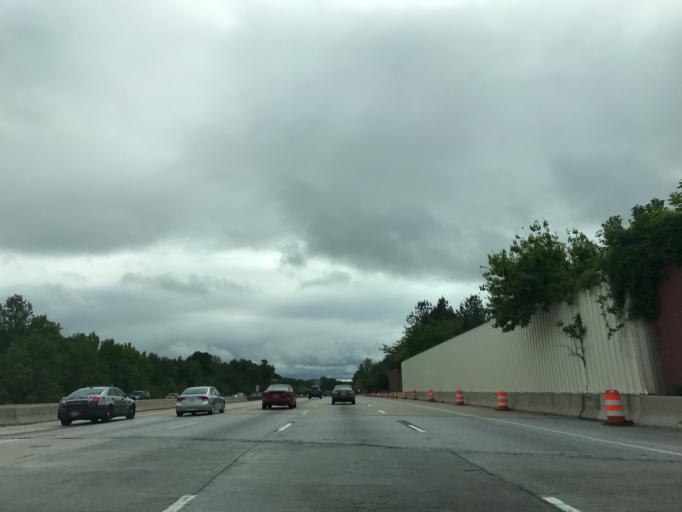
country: US
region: Maryland
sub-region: Prince George's County
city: Bowie
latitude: 38.9511
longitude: -76.7499
